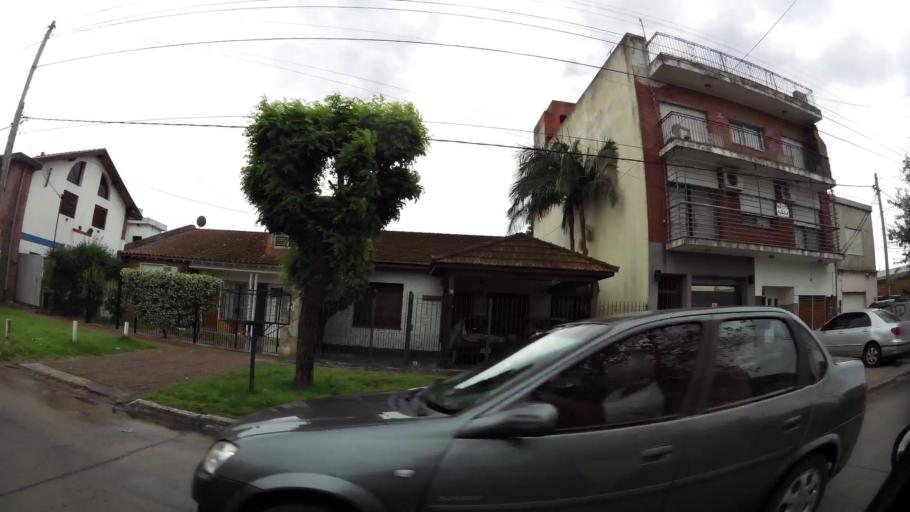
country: AR
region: Buenos Aires
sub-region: Partido de Quilmes
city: Quilmes
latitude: -34.7518
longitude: -58.2262
